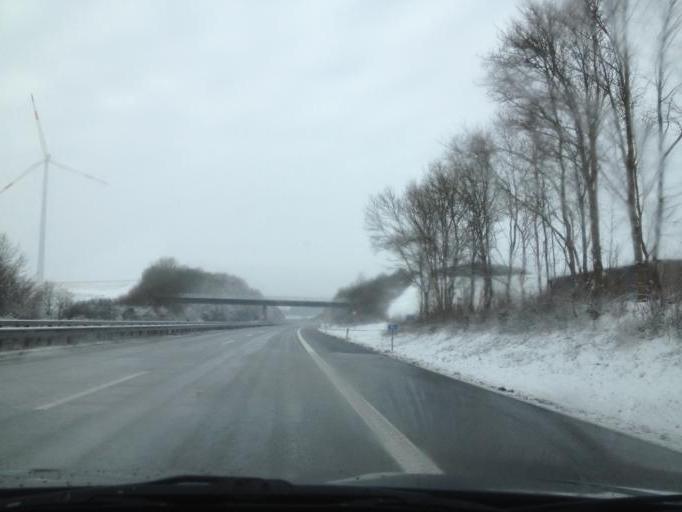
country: DE
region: Rheinland-Pfalz
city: Walshausen
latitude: 49.2154
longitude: 7.4970
